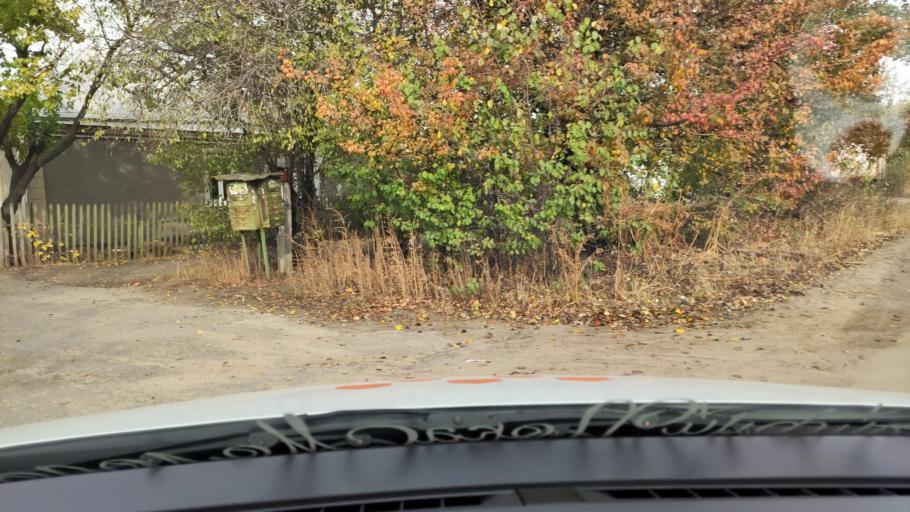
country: RU
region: Voronezj
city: Voronezh
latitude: 51.6816
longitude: 39.1372
